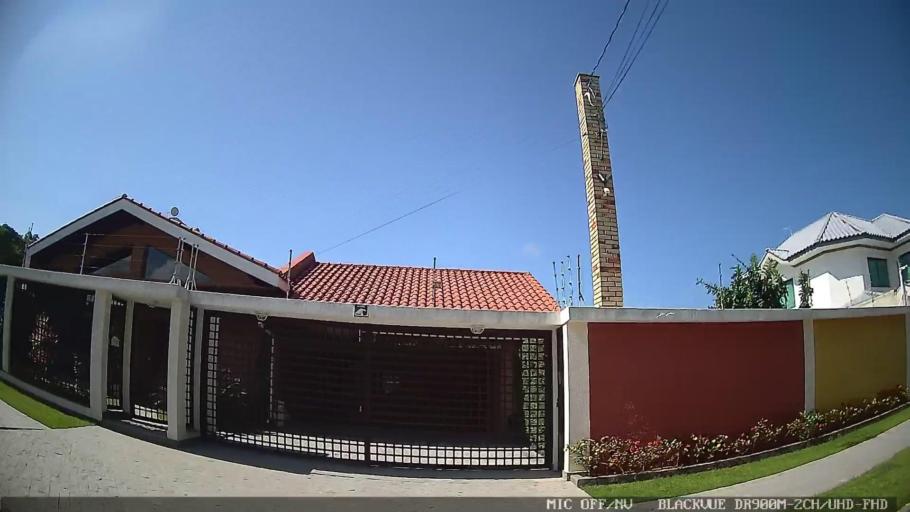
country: BR
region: Sao Paulo
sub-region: Peruibe
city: Peruibe
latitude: -24.3166
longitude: -46.9907
